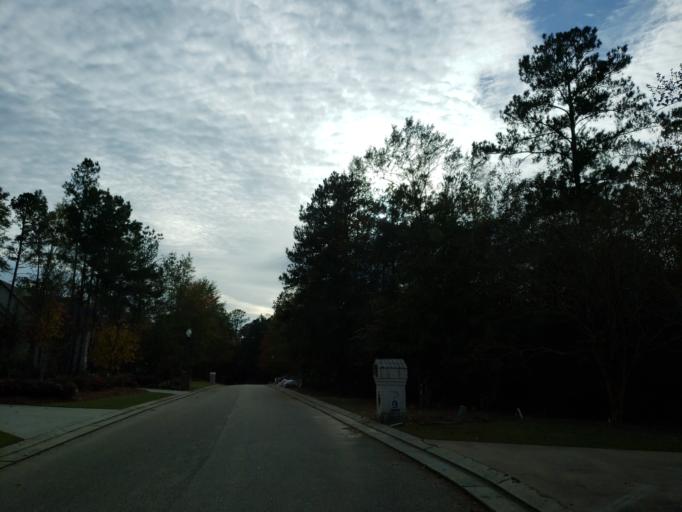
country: US
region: Mississippi
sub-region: Lamar County
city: West Hattiesburg
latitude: 31.2986
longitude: -89.3457
